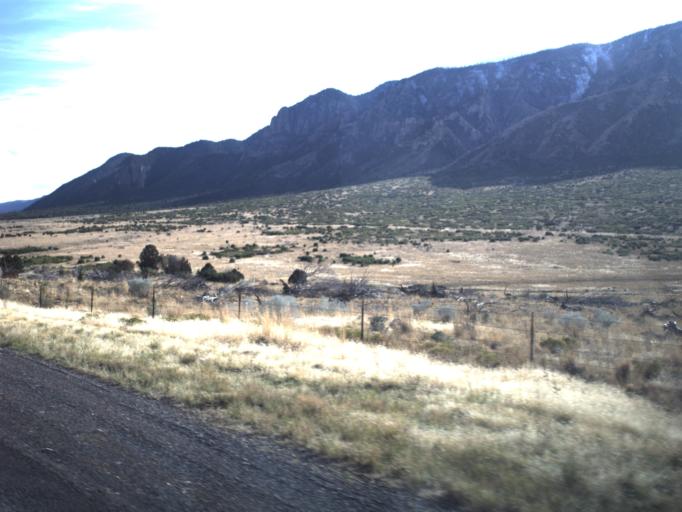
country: US
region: Utah
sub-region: Sanpete County
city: Gunnison
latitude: 39.1679
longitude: -112.0744
